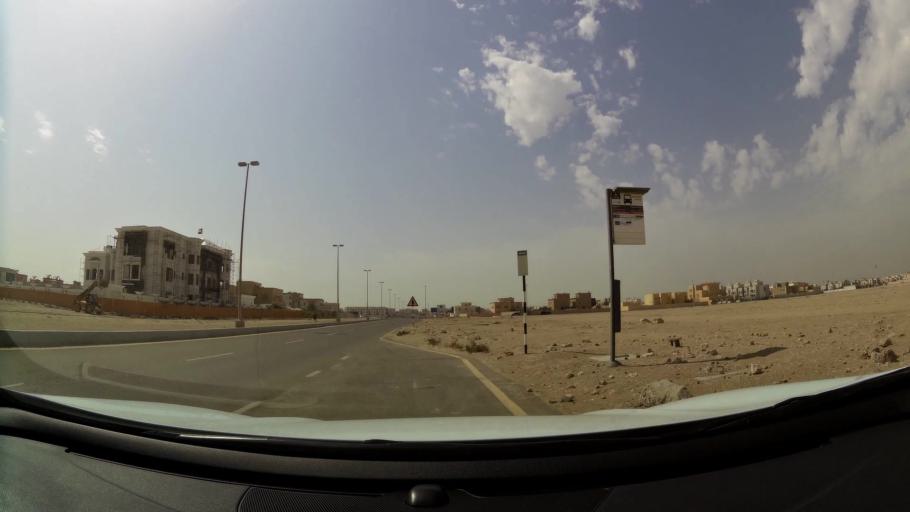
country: AE
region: Abu Dhabi
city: Abu Dhabi
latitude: 24.3323
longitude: 54.5561
